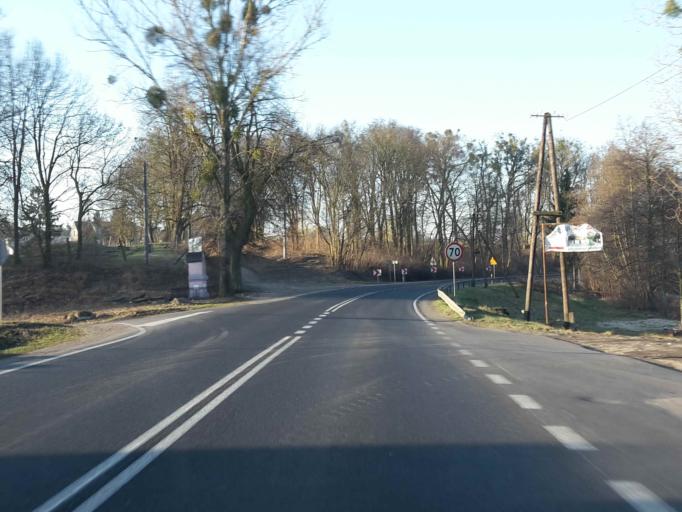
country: PL
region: Kujawsko-Pomorskie
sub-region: Powiat brodnicki
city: Bobrowo
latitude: 53.2440
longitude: 19.2995
